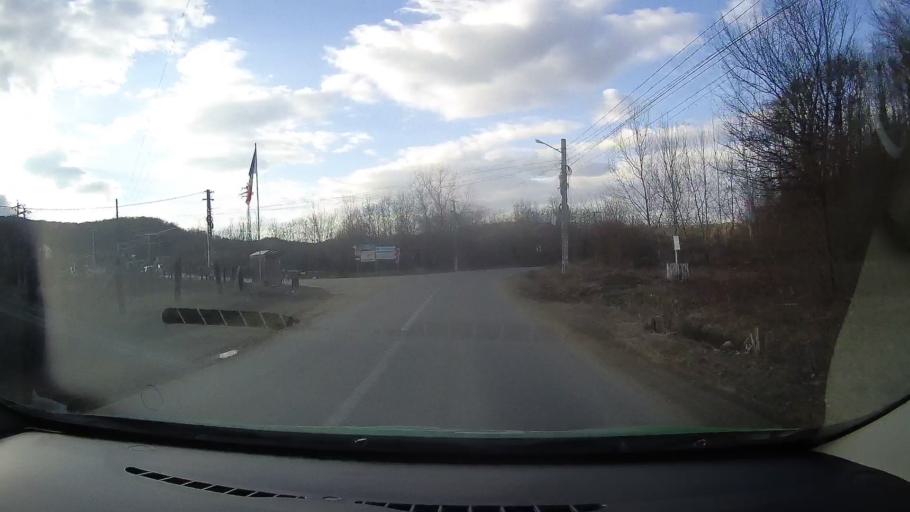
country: RO
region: Dambovita
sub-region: Comuna Ocnita
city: Ocnita
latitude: 44.9645
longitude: 25.5479
